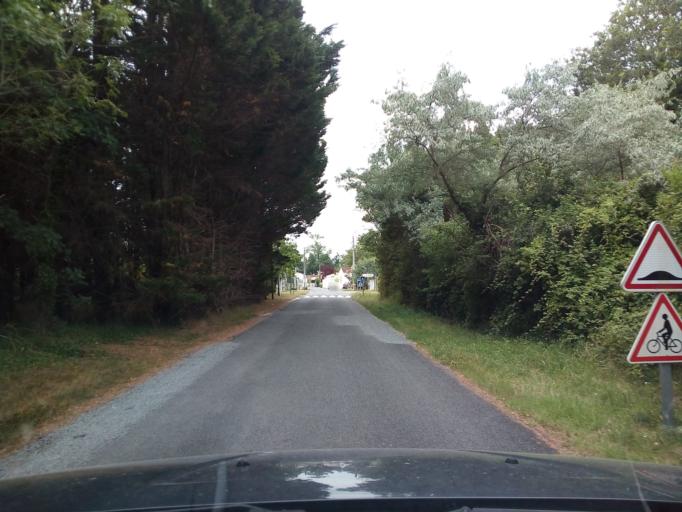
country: FR
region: Poitou-Charentes
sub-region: Departement de la Charente-Maritime
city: Dolus-d'Oleron
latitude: 45.9249
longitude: -1.2715
